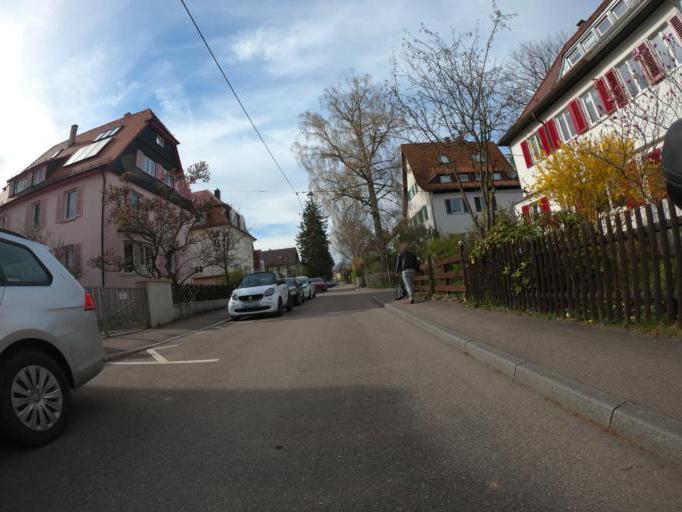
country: DE
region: Baden-Wuerttemberg
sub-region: Regierungsbezirk Stuttgart
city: Stuttgart
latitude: 48.7503
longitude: 9.1830
